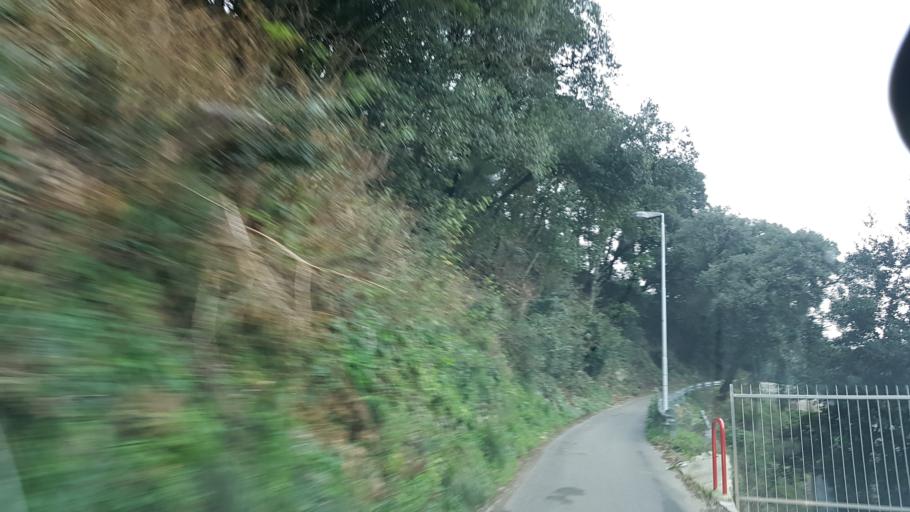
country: IT
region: Liguria
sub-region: Provincia di Savona
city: Valleggia
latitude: 44.3045
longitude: 8.4447
